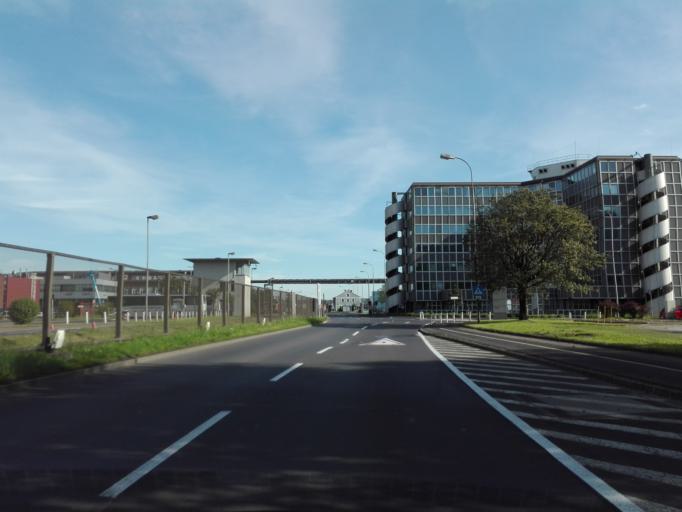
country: AT
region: Upper Austria
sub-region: Linz Stadt
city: Linz
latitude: 48.2758
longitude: 14.3227
